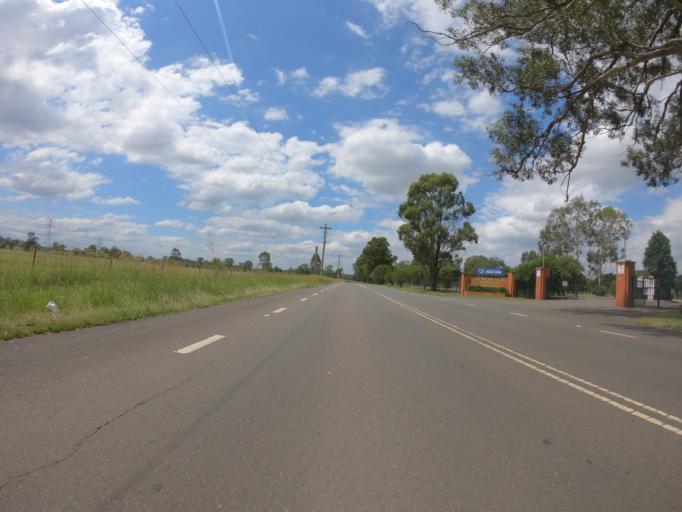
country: AU
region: New South Wales
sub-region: Penrith Municipality
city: Kingswood Park
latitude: -33.8106
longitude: 150.7617
